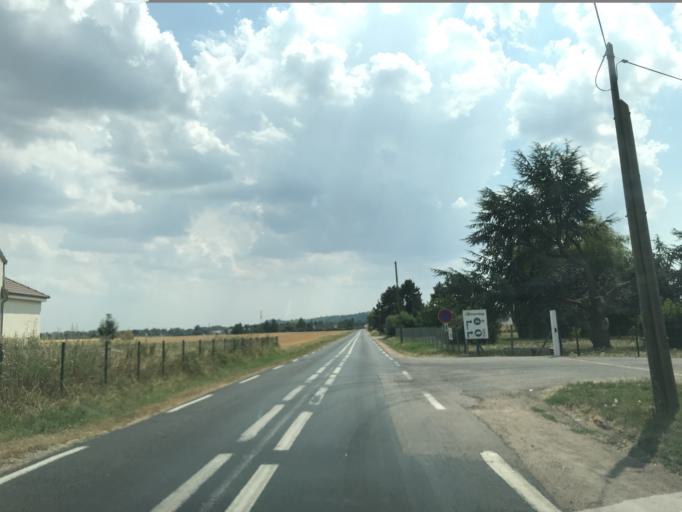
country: FR
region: Haute-Normandie
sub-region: Departement de l'Eure
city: Bueil
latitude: 48.9227
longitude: 1.4429
